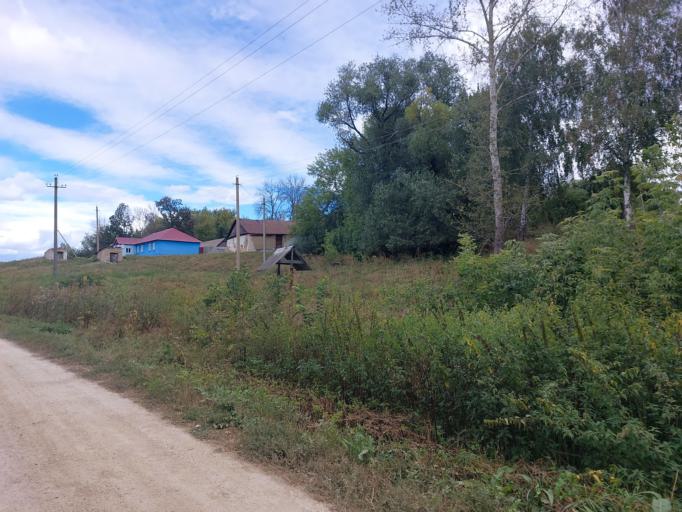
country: RU
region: Lipetsk
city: Terbuny
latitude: 52.2635
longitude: 38.2049
